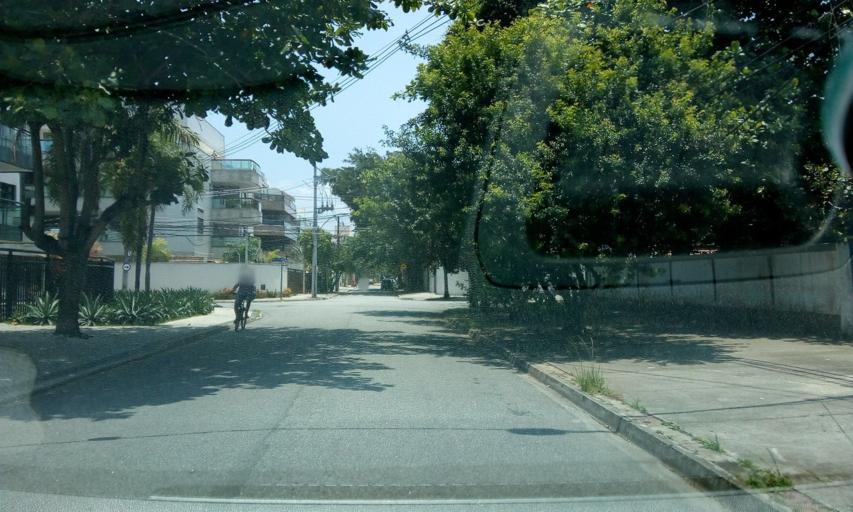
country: BR
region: Rio de Janeiro
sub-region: Nilopolis
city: Nilopolis
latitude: -23.0205
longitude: -43.4656
